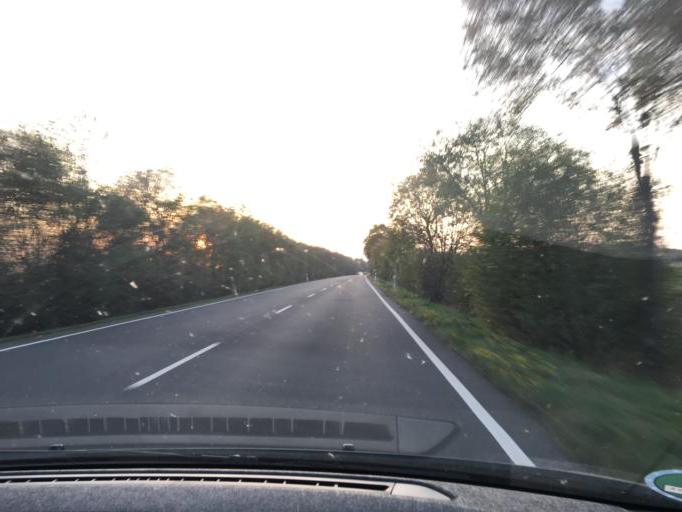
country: DE
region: North Rhine-Westphalia
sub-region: Regierungsbezirk Koln
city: Kerpen
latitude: 50.8237
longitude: 6.7059
